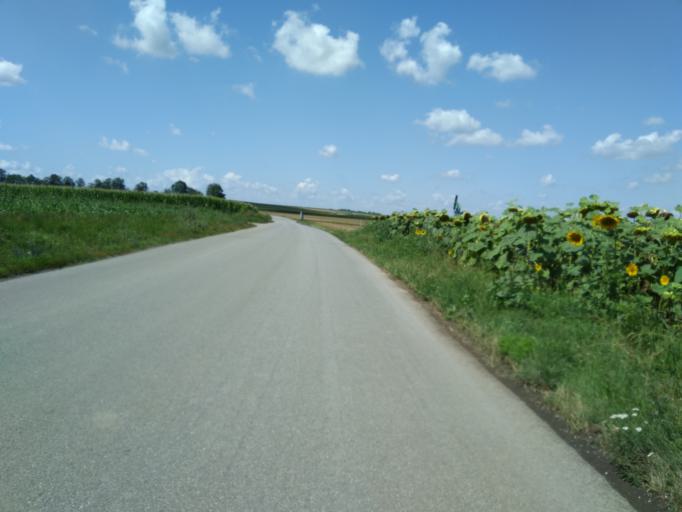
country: AT
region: Lower Austria
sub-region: Politischer Bezirk Ganserndorf
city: Auersthal
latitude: 48.3763
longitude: 16.6708
